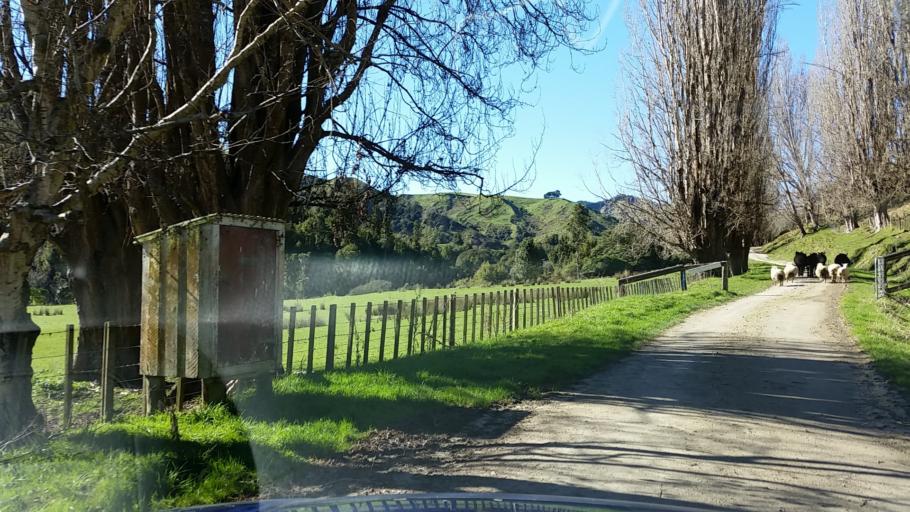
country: NZ
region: Manawatu-Wanganui
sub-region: Wanganui District
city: Wanganui
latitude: -39.5332
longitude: 174.9287
